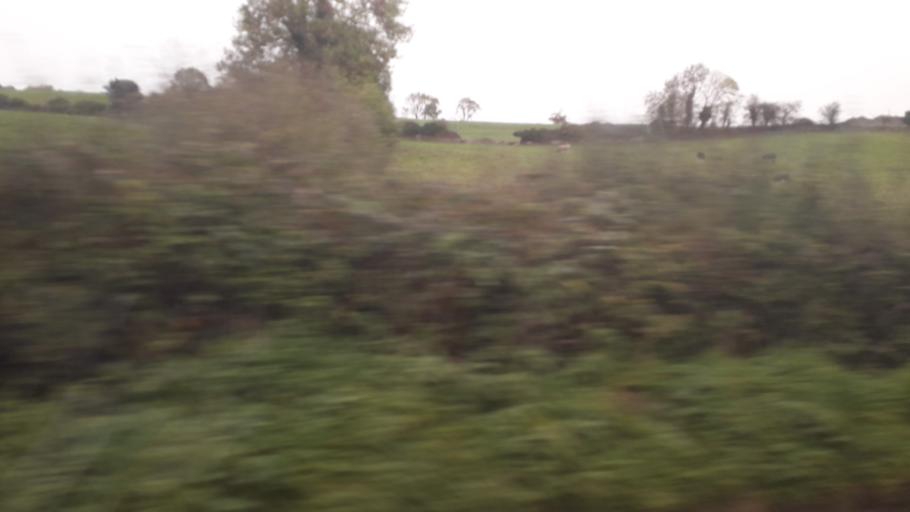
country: IE
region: Leinster
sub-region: Uibh Fhaili
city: Birr
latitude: 52.9776
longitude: -7.9629
